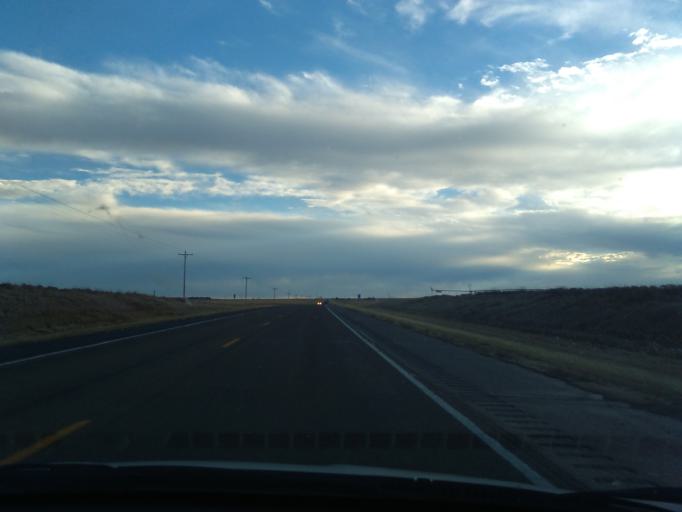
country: US
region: Nebraska
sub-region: Phelps County
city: Holdrege
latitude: 40.4074
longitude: -99.3697
